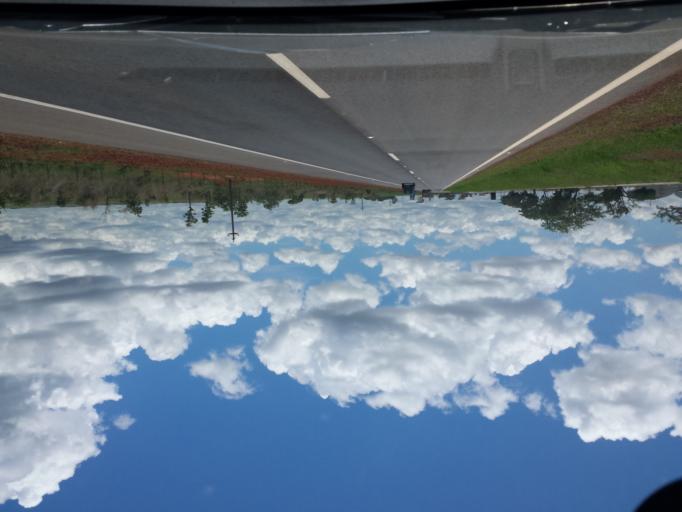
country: BR
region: Goias
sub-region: Cristalina
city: Cristalina
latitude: -16.7012
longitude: -47.6917
